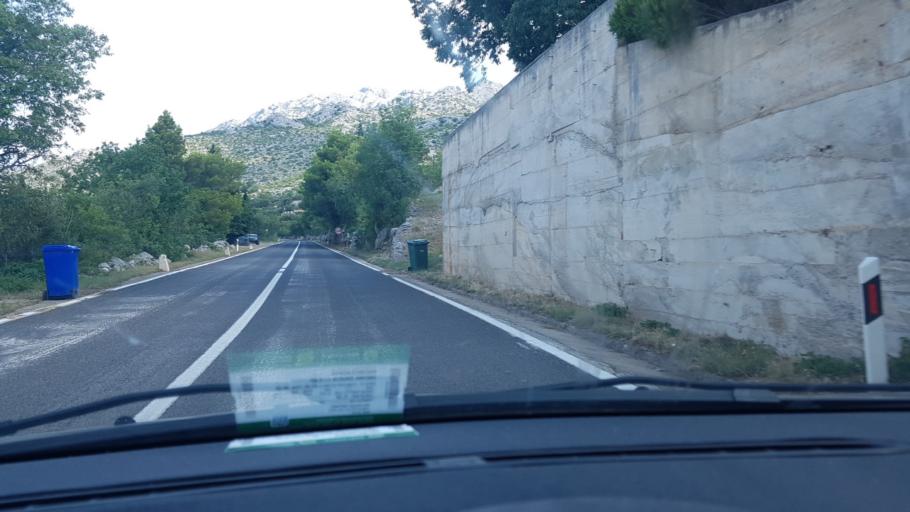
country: HR
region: Zadarska
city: Starigrad
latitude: 44.3097
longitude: 15.4242
